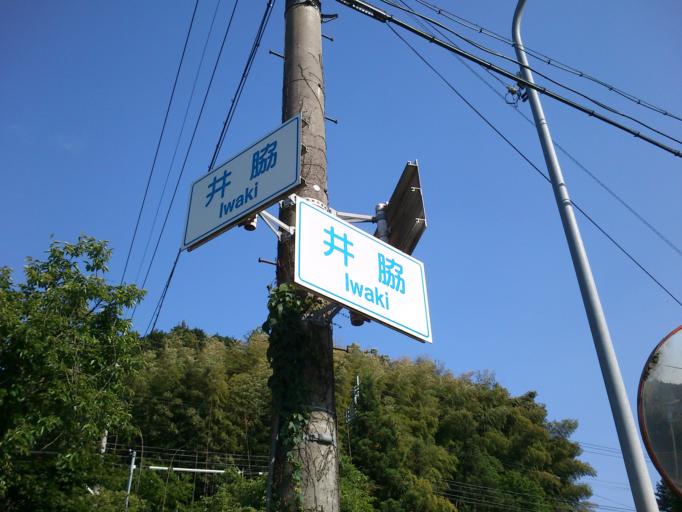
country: JP
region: Kyoto
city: Ayabe
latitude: 35.1936
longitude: 135.3619
